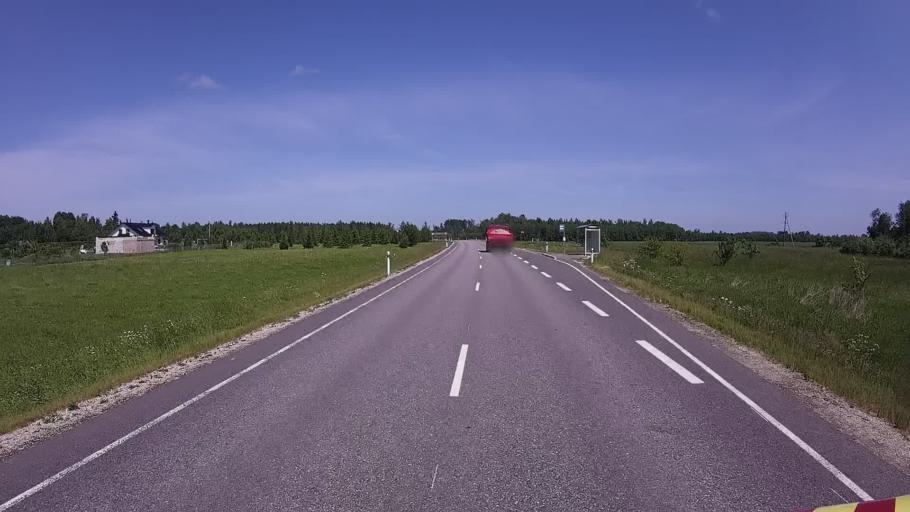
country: EE
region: Tartu
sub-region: Tartu linn
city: Tartu
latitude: 58.3976
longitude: 26.8955
